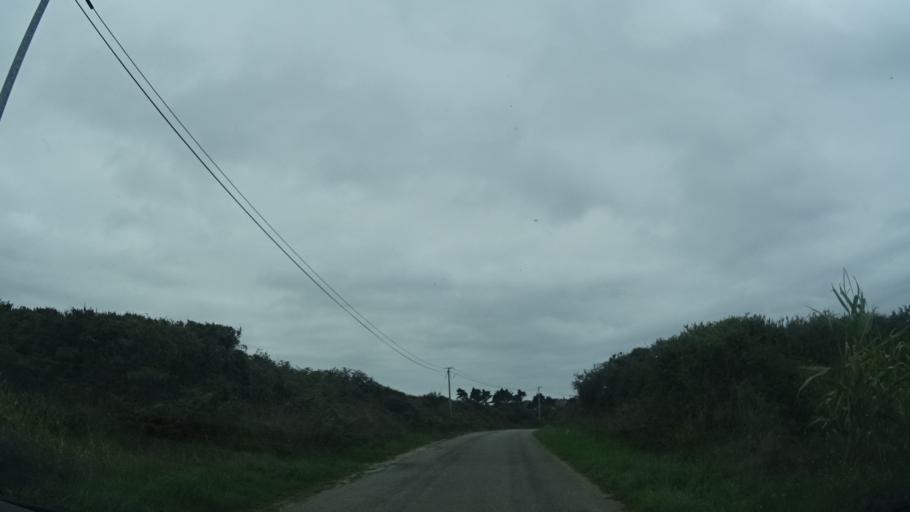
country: FR
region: Brittany
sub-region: Departement du Finistere
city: Lampaul-Plouarzel
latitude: 48.4529
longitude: -4.7570
